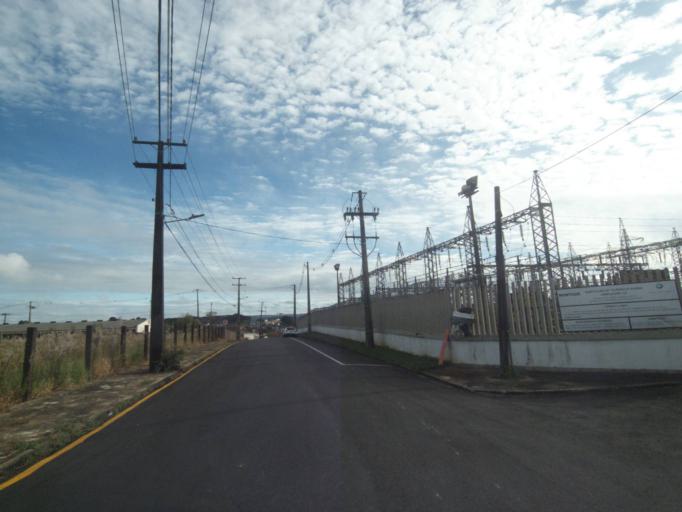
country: BR
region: Parana
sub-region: Telemaco Borba
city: Telemaco Borba
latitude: -24.3397
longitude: -50.6110
